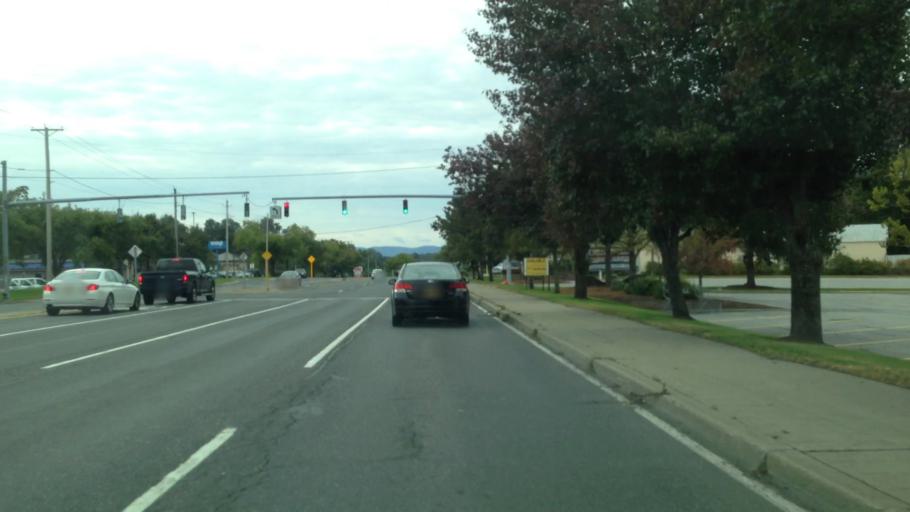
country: US
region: New York
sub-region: Dutchess County
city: Spackenkill
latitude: 41.6648
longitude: -73.9301
